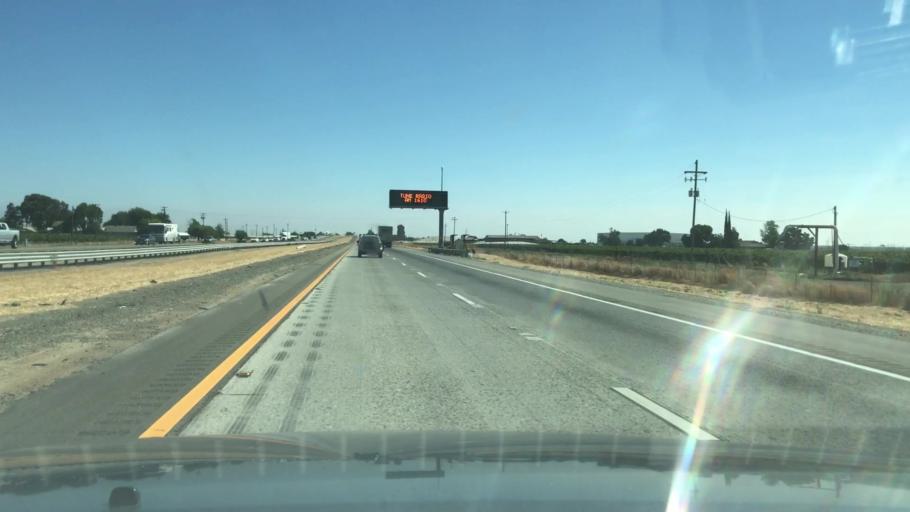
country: US
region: California
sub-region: San Joaquin County
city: Thornton
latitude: 38.1689
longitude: -121.4000
